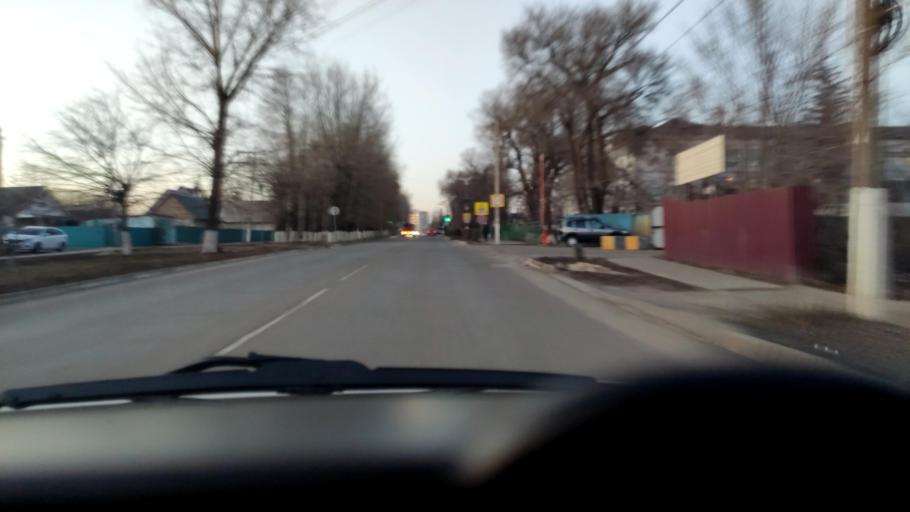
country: RU
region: Voronezj
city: Semiluki
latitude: 51.6942
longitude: 39.0322
